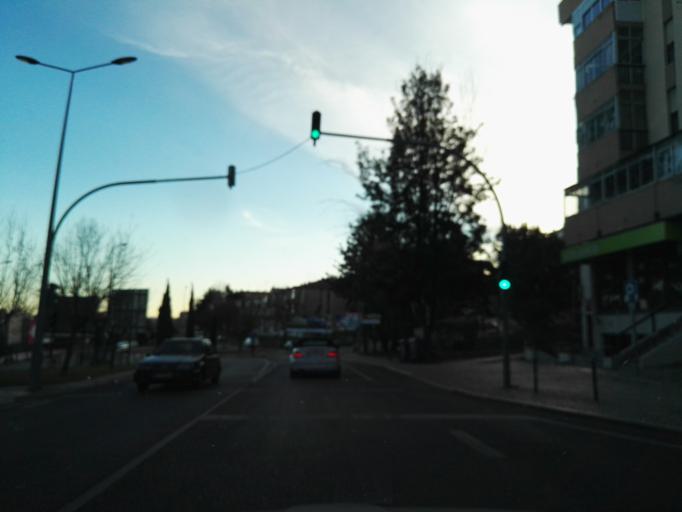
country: PT
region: Lisbon
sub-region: Vila Franca de Xira
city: Povoa de Santa Iria
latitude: 38.8556
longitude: -9.0712
